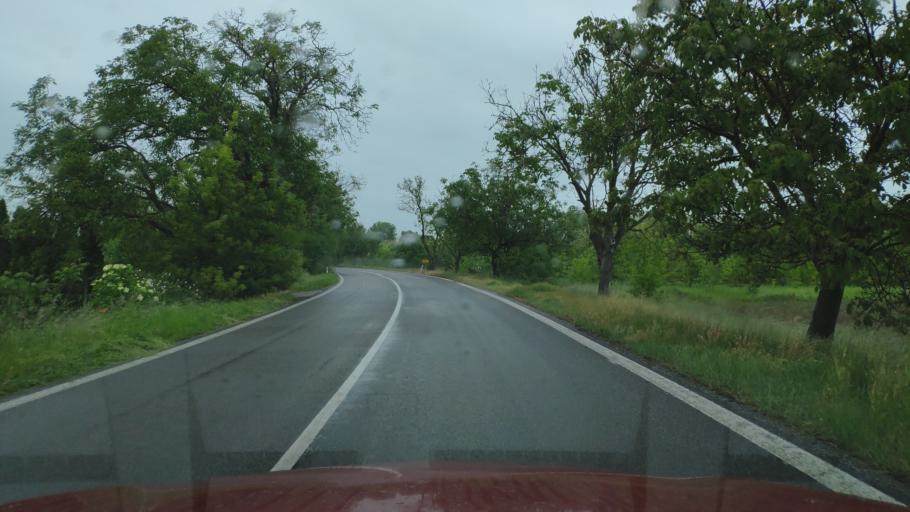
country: HU
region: Borsod-Abauj-Zemplen
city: Karcsa
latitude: 48.3992
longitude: 21.8104
